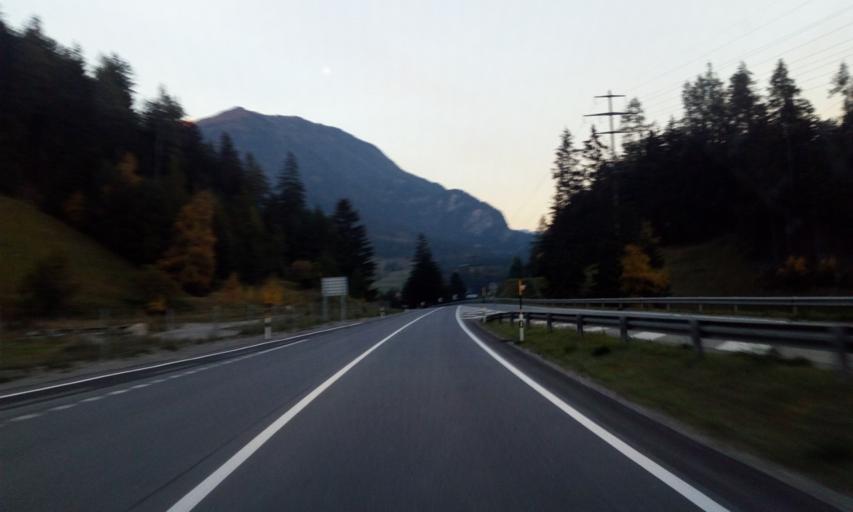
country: CH
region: Grisons
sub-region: Albula District
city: Tiefencastel
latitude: 46.6708
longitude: 9.5645
